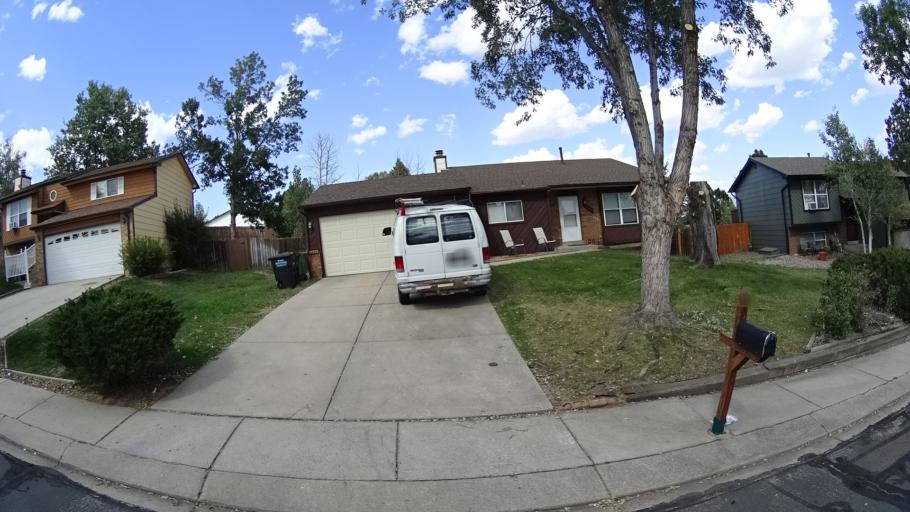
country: US
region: Colorado
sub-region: El Paso County
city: Cimarron Hills
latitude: 38.8748
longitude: -104.7263
